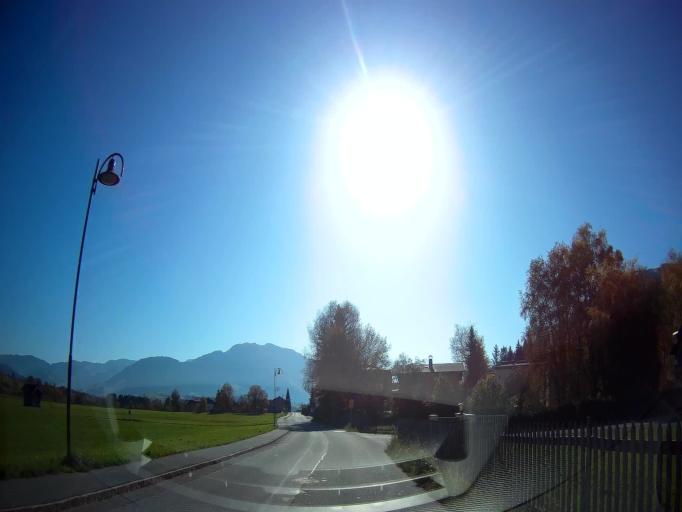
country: AT
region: Salzburg
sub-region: Politischer Bezirk Zell am See
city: Saalfelden am Steinernen Meer
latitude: 47.4429
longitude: 12.8180
